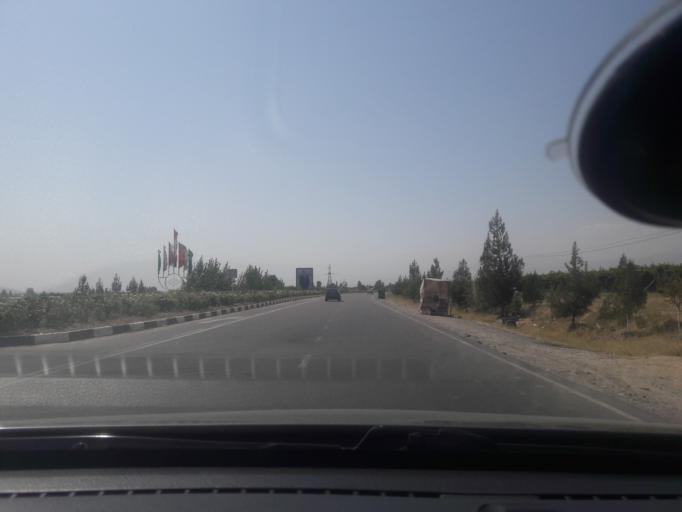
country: TJ
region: Republican Subordination
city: Hisor
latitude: 38.5599
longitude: 68.4576
